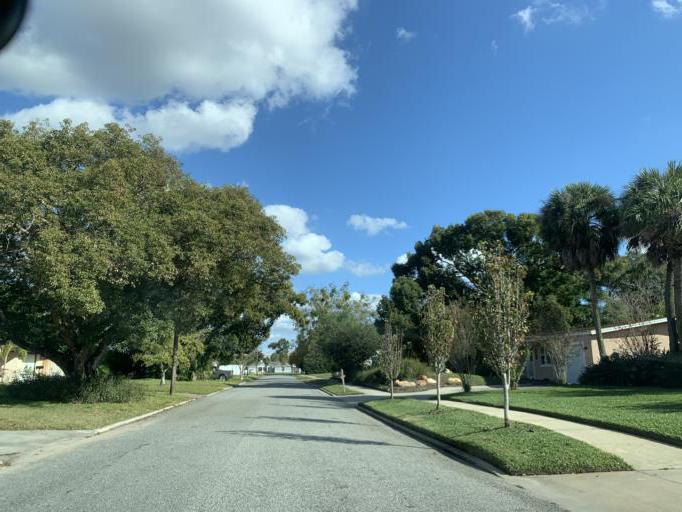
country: US
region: Florida
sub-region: Orange County
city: Eatonville
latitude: 28.6095
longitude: -81.3915
